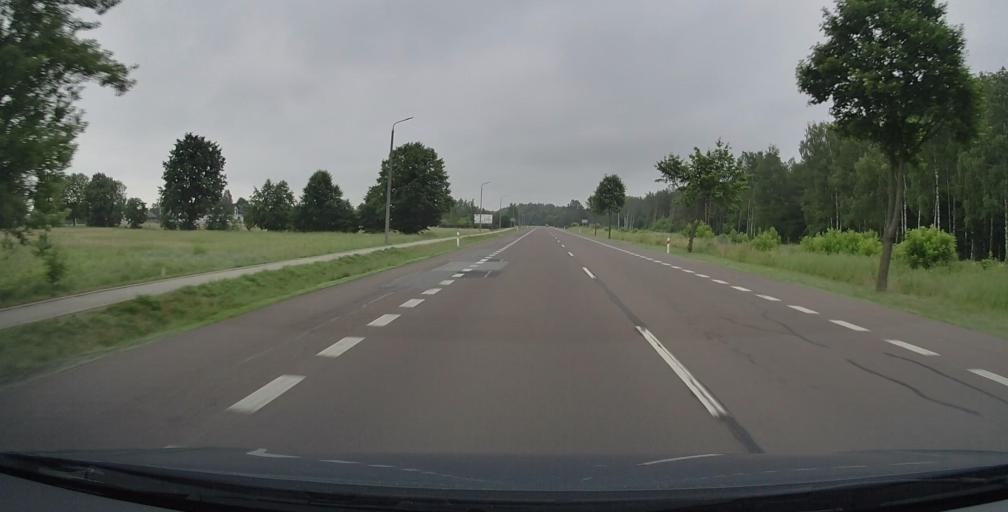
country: PL
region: Lublin Voivodeship
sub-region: Powiat bialski
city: Terespol
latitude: 52.0425
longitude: 23.5296
